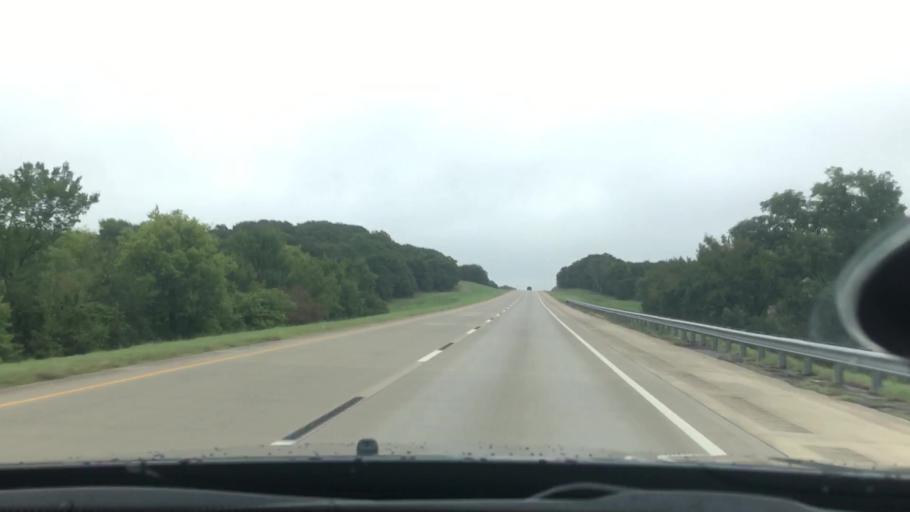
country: US
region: Oklahoma
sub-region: Okfuskee County
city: Boley
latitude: 35.3844
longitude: -96.5768
